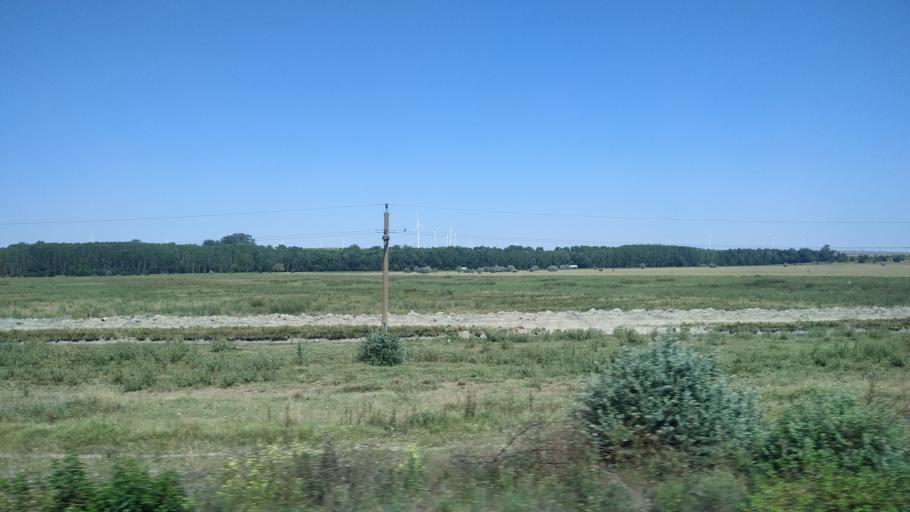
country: RO
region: Constanta
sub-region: Comuna Mircea Voda
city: Mircea Voda
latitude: 44.2647
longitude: 28.1588
